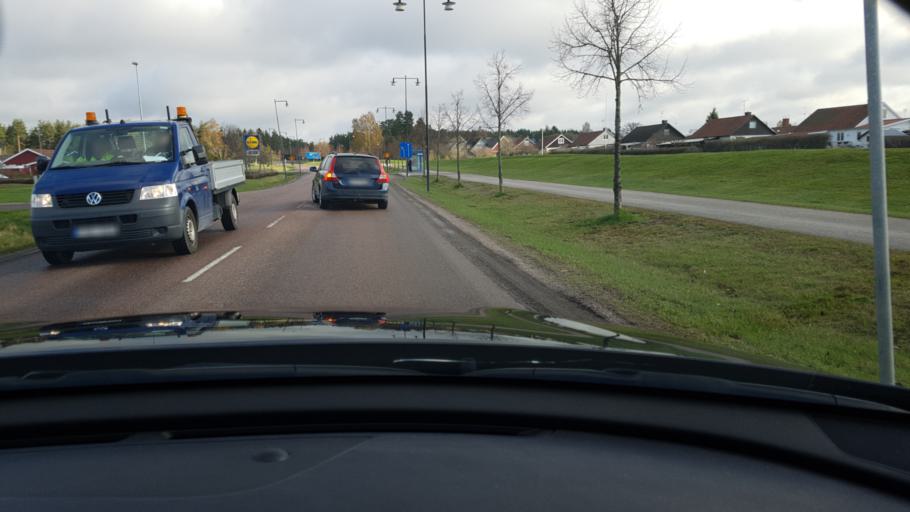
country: SE
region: Vaestmanland
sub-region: Arboga Kommun
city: Arboga
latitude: 59.4013
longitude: 15.8324
